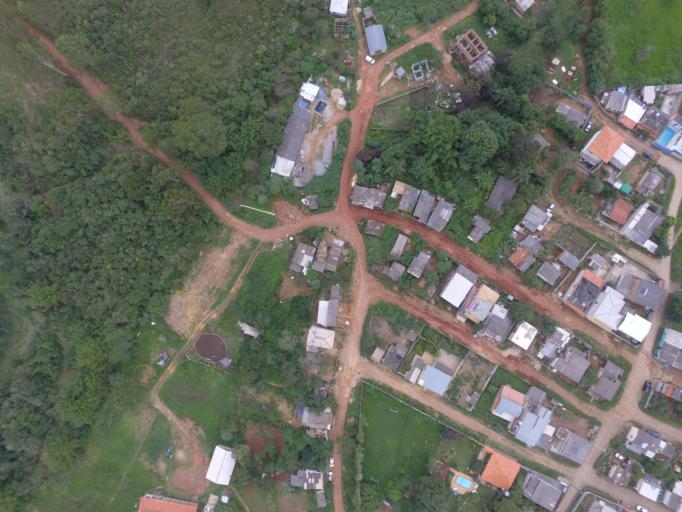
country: BR
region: Minas Gerais
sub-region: Tiradentes
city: Tiradentes
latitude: -21.0493
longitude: -44.0891
